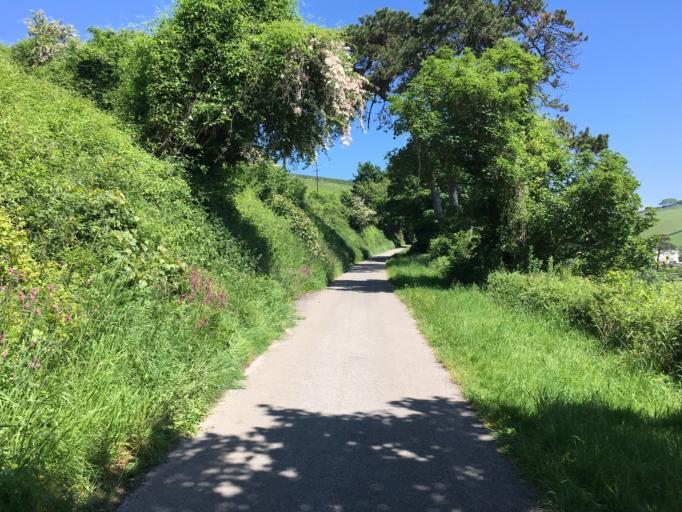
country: GB
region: England
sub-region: Devon
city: Dartmouth
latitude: 50.3442
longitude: -3.5577
